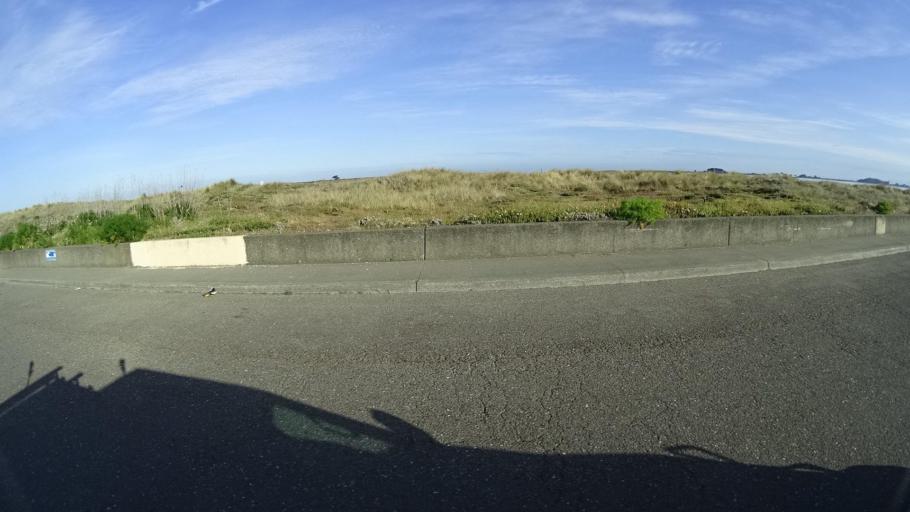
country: US
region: California
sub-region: Humboldt County
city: Humboldt Hill
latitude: 40.7410
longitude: -124.2170
